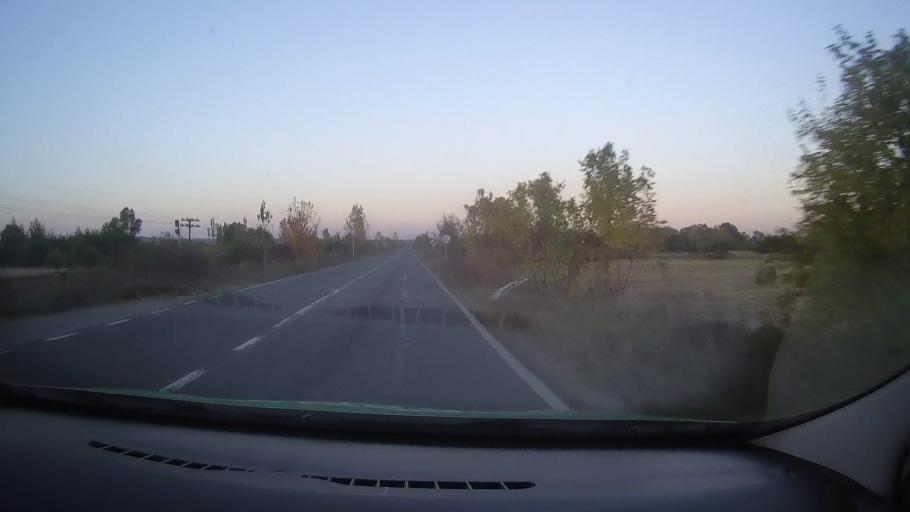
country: RO
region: Timis
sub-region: Comuna Dumbrava
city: Dumbrava
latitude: 45.8407
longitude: 22.1444
